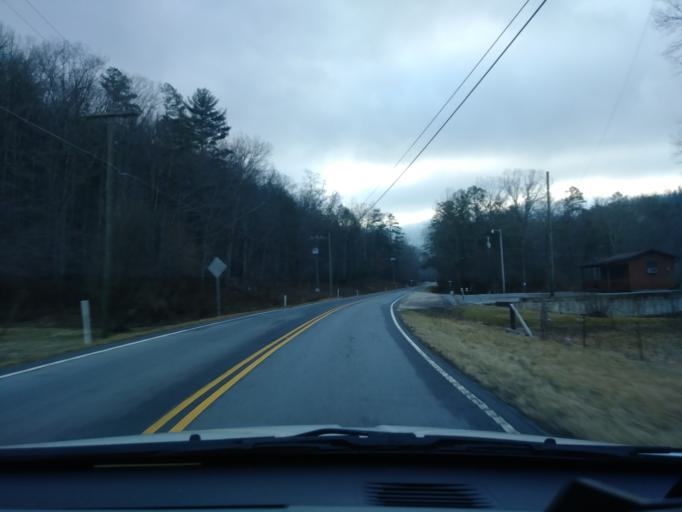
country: US
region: Tennessee
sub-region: Unicoi County
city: Unicoi
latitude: 36.1835
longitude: -82.3260
